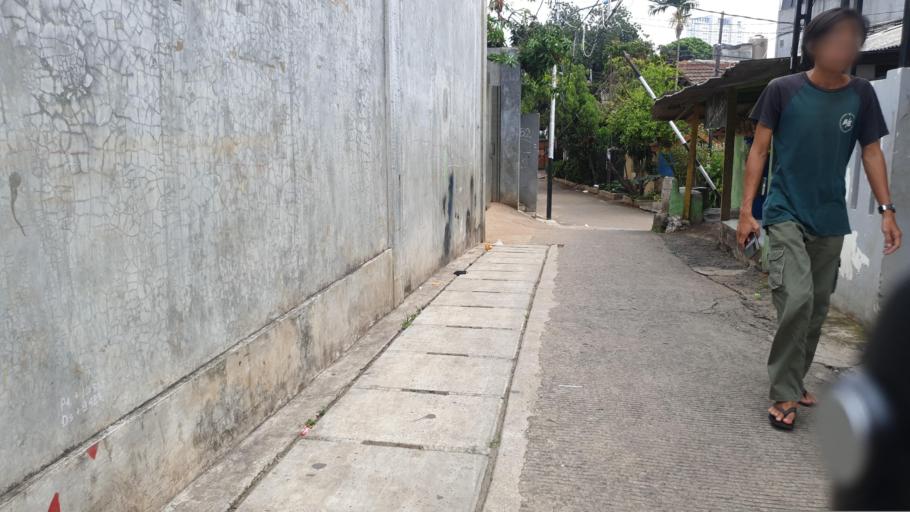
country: ID
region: West Java
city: Ciputat
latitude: -6.1956
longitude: 106.7543
